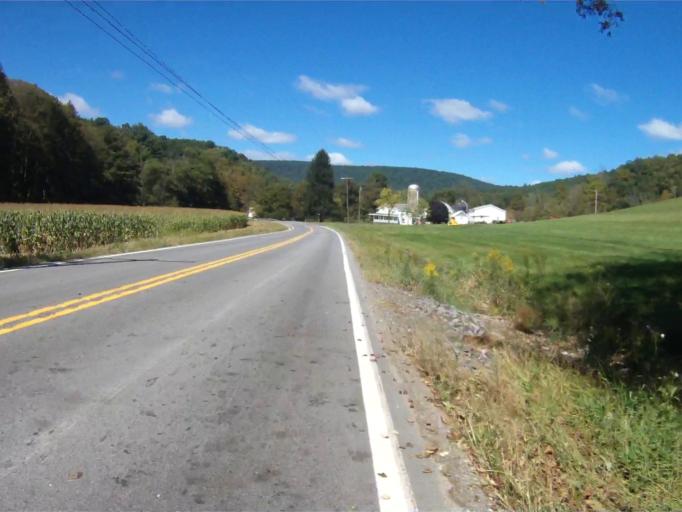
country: US
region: Pennsylvania
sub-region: Centre County
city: Milesburg
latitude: 40.9220
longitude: -77.8977
